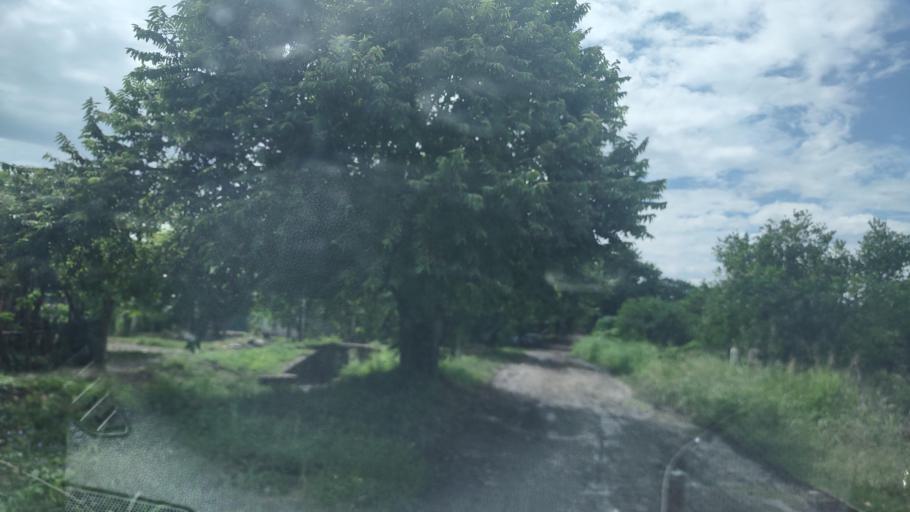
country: MX
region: Veracruz
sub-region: Atzalan
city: Colonias Pedernales
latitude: 20.0578
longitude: -97.0109
